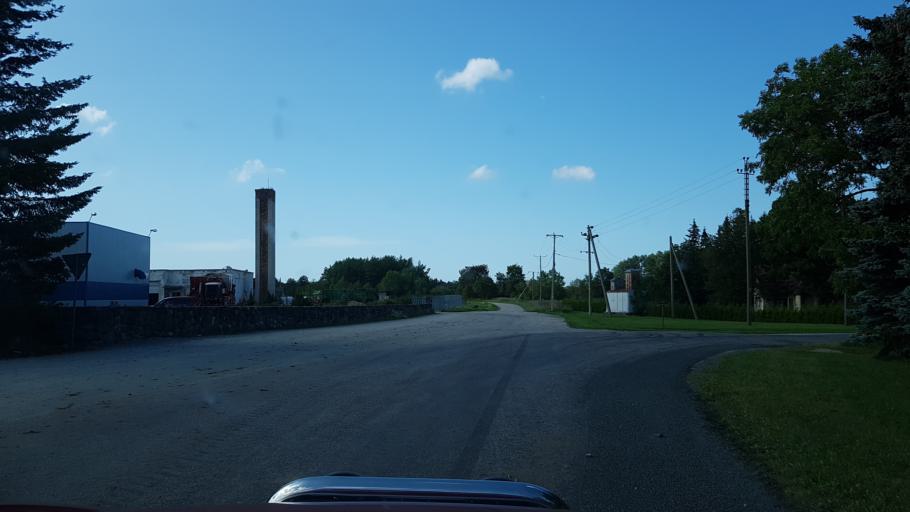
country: EE
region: Harju
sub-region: Paldiski linn
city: Paldiski
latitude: 59.2367
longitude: 24.0193
